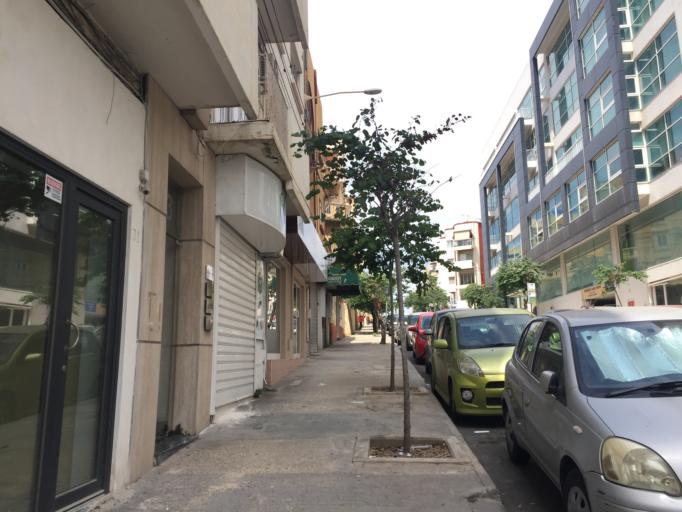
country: MT
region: Ta' Xbiex
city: Ta' Xbiex
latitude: 35.8976
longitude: 14.4937
